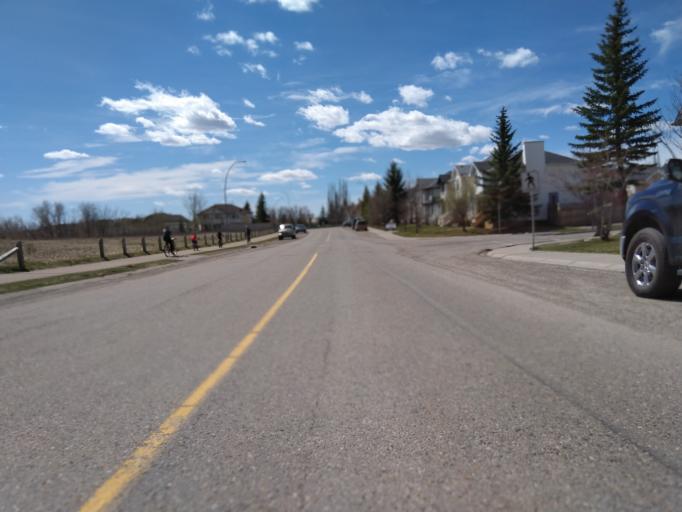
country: CA
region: Alberta
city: Calgary
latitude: 51.1275
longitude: -114.2436
